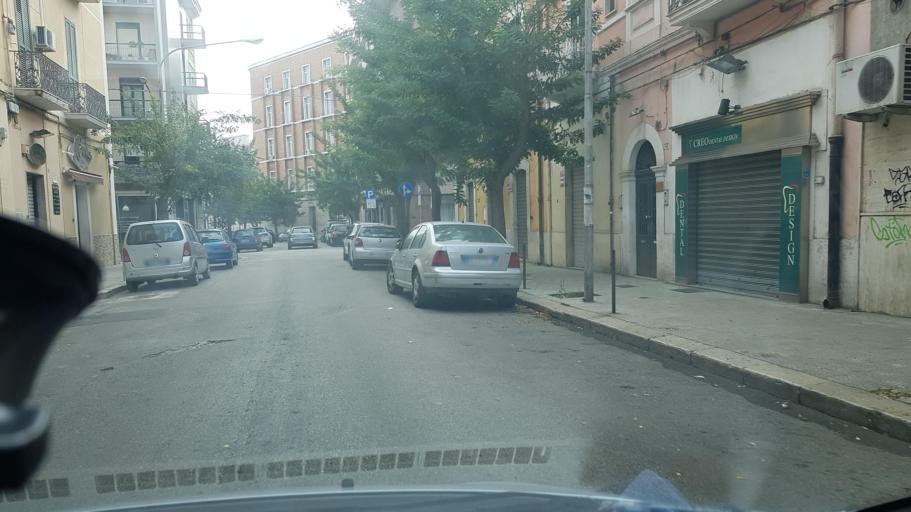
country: IT
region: Apulia
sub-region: Provincia di Foggia
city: Foggia
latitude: 41.4598
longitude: 15.5526
